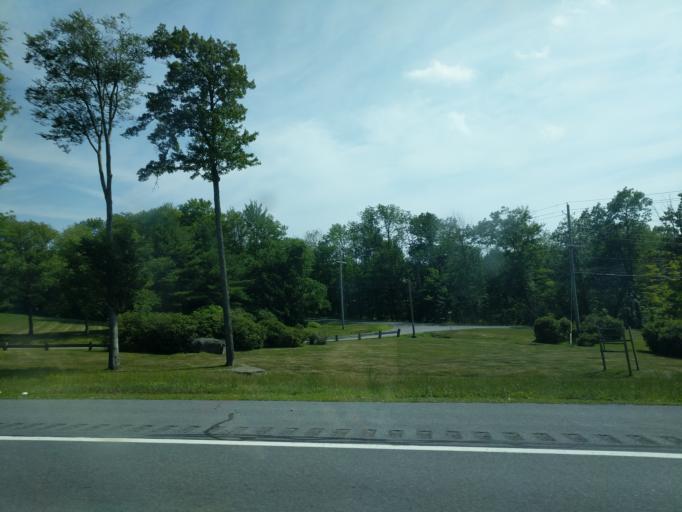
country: US
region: New York
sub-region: Sullivan County
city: Rock Hill
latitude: 41.6210
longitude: -74.5873
